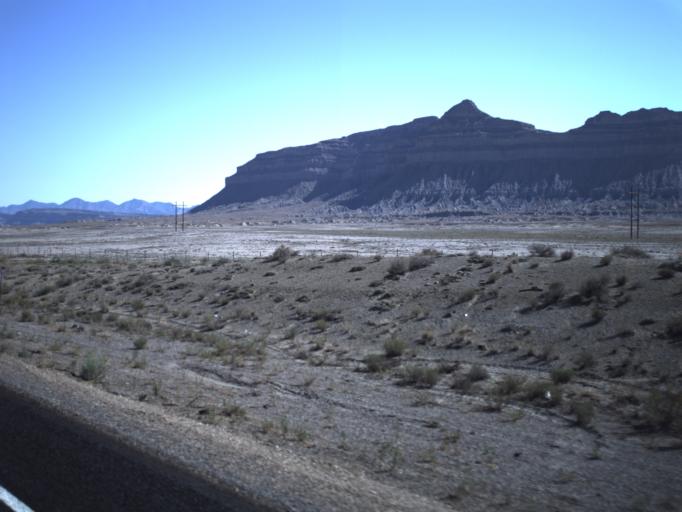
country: US
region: Utah
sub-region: Carbon County
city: East Carbon City
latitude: 39.1493
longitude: -110.3374
